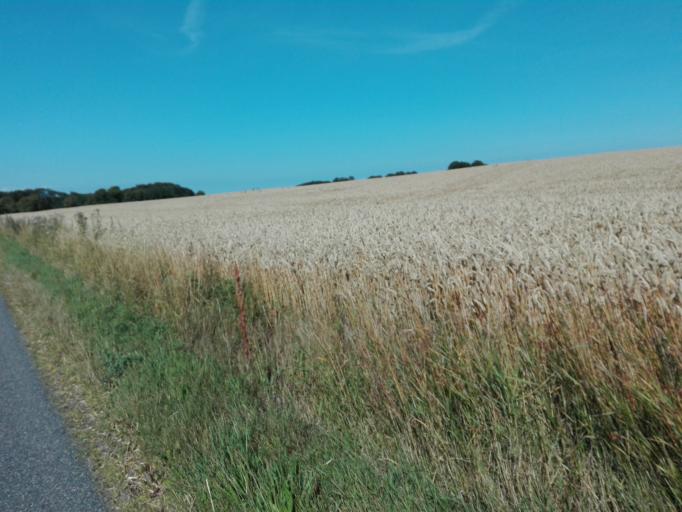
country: DK
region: Central Jutland
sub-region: Odder Kommune
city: Odder
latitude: 55.9579
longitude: 10.1134
